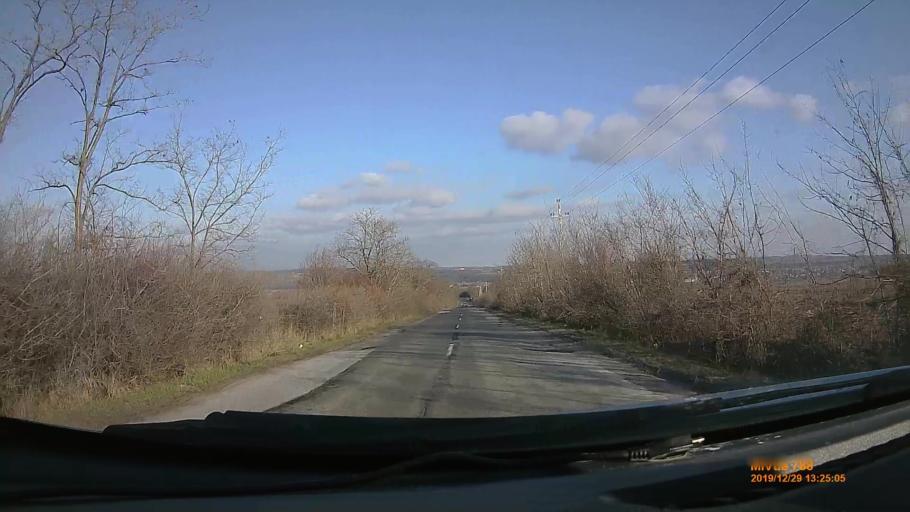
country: HU
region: Heves
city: Verpelet
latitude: 47.8464
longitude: 20.1901
